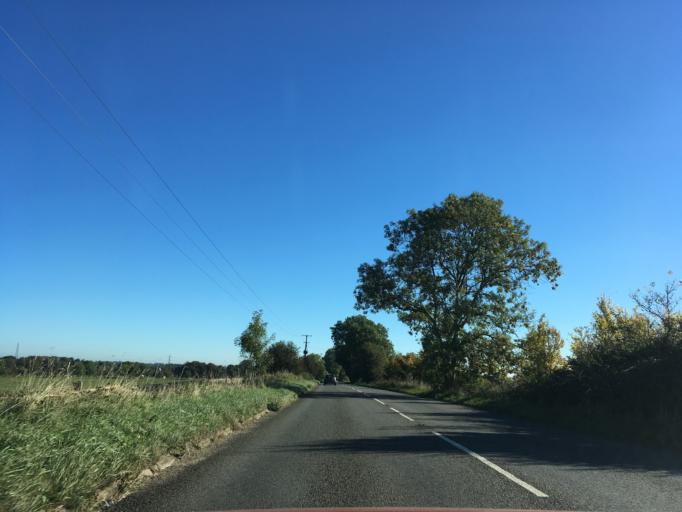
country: GB
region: England
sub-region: Wiltshire
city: Colerne
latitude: 51.4682
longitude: -2.2707
